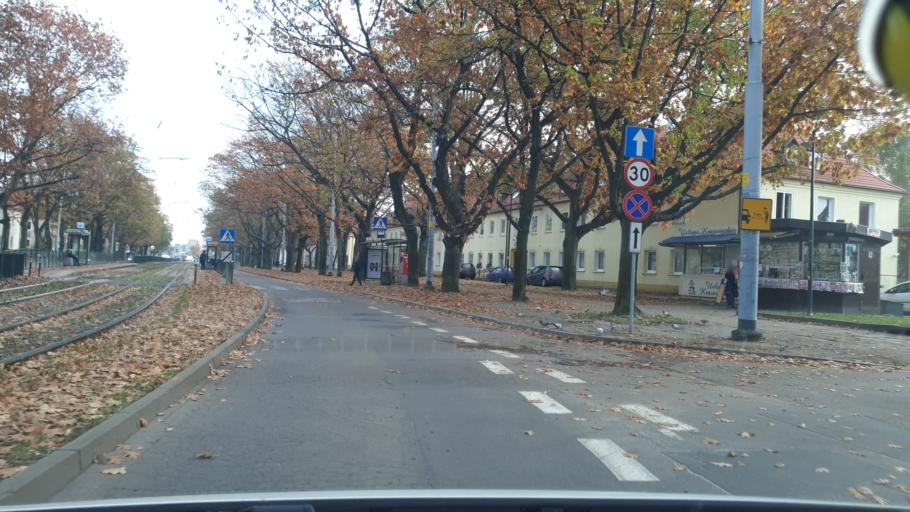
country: PL
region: Pomeranian Voivodeship
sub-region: Sopot
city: Sopot
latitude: 54.3868
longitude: 18.5843
